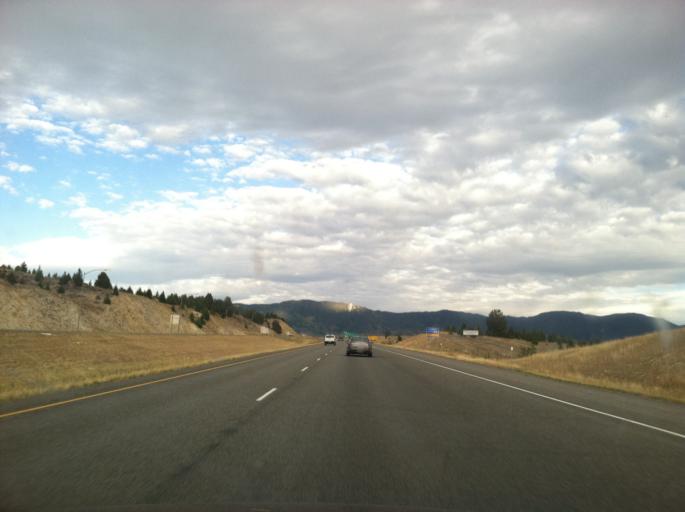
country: US
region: Montana
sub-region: Silver Bow County
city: Butte
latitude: 46.0055
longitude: -112.5871
